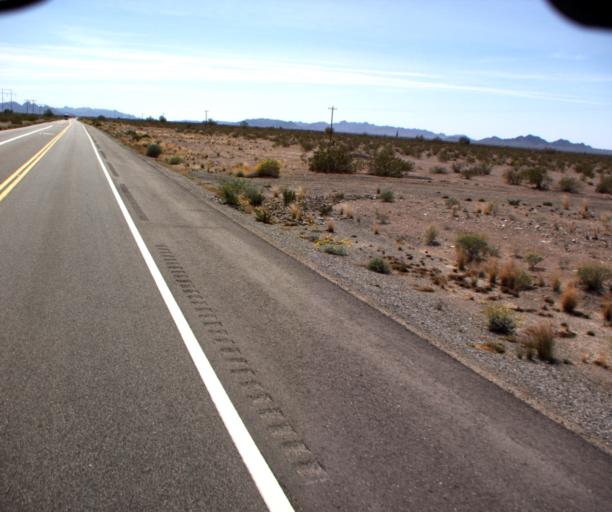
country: US
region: Arizona
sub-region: La Paz County
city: Quartzsite
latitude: 33.4433
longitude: -114.2171
